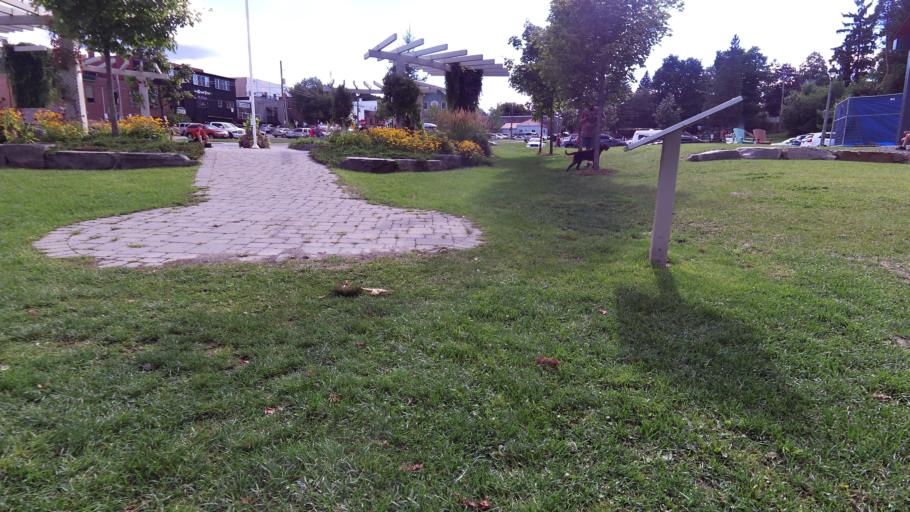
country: CA
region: Ontario
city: Huntsville
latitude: 45.3276
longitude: -79.2177
